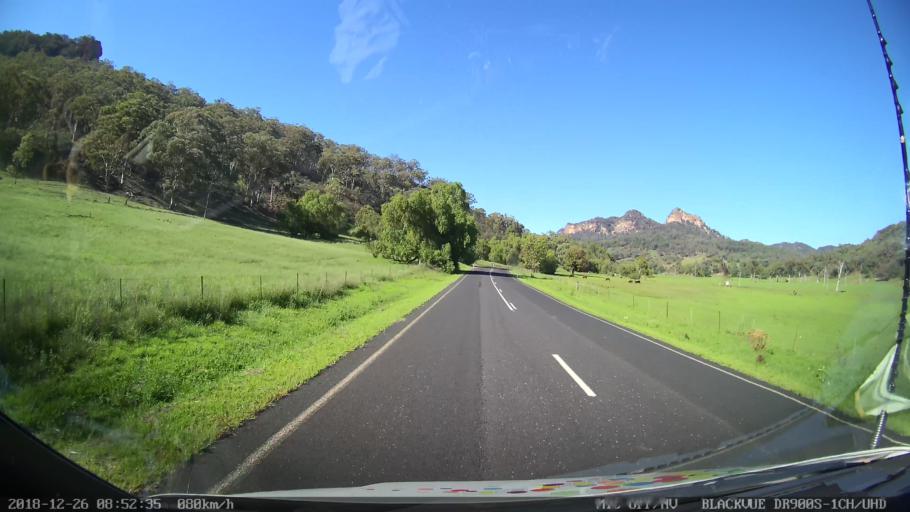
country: AU
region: New South Wales
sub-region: Mid-Western Regional
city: Kandos
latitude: -32.5981
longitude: 150.0855
